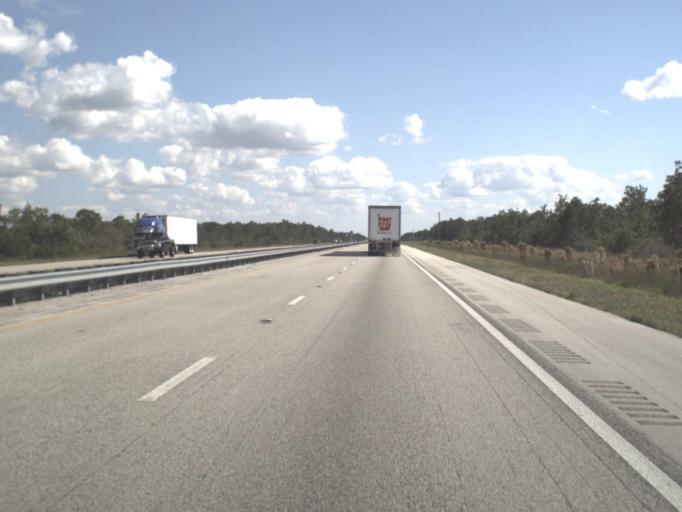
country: US
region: Florida
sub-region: Osceola County
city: Saint Cloud
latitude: 27.9913
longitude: -81.1293
